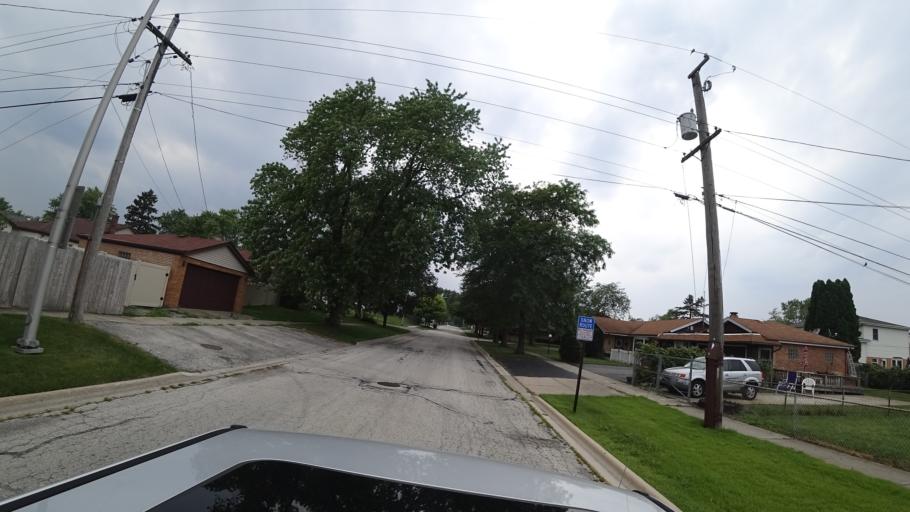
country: US
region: Illinois
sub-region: Cook County
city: Oak Lawn
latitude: 41.6924
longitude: -87.7610
